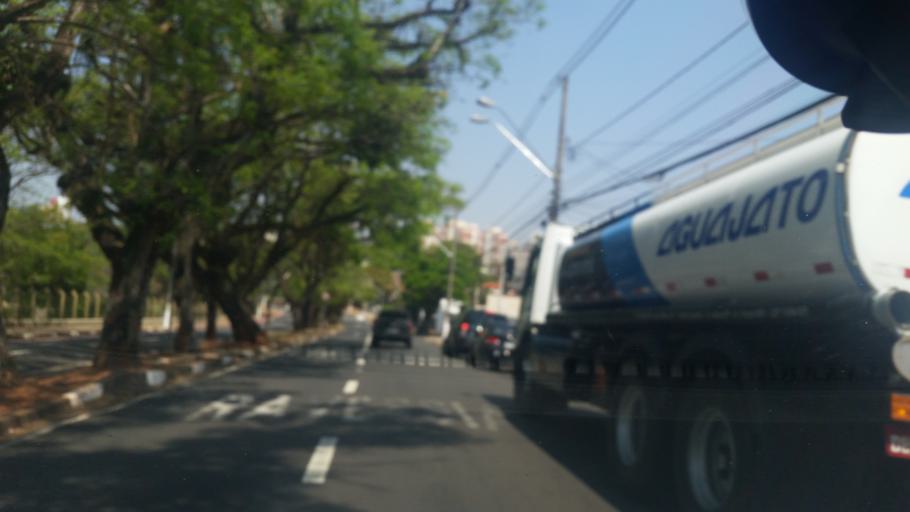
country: BR
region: Sao Paulo
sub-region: Campinas
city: Campinas
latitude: -22.8777
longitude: -47.0624
